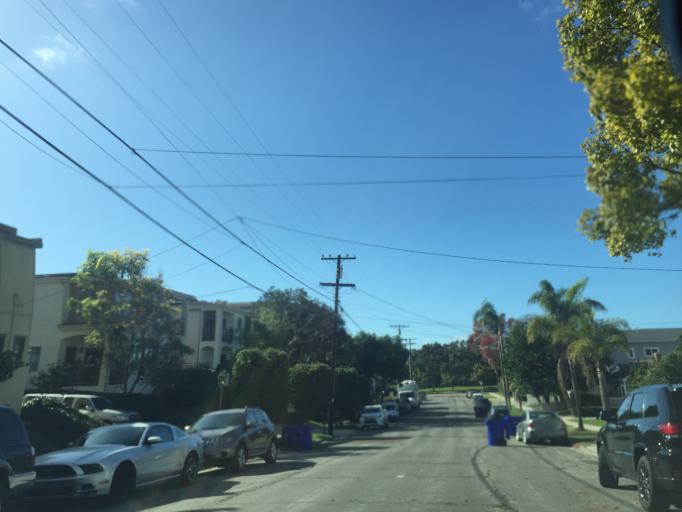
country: US
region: California
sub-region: San Diego County
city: La Jolla
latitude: 32.7924
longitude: -117.2426
